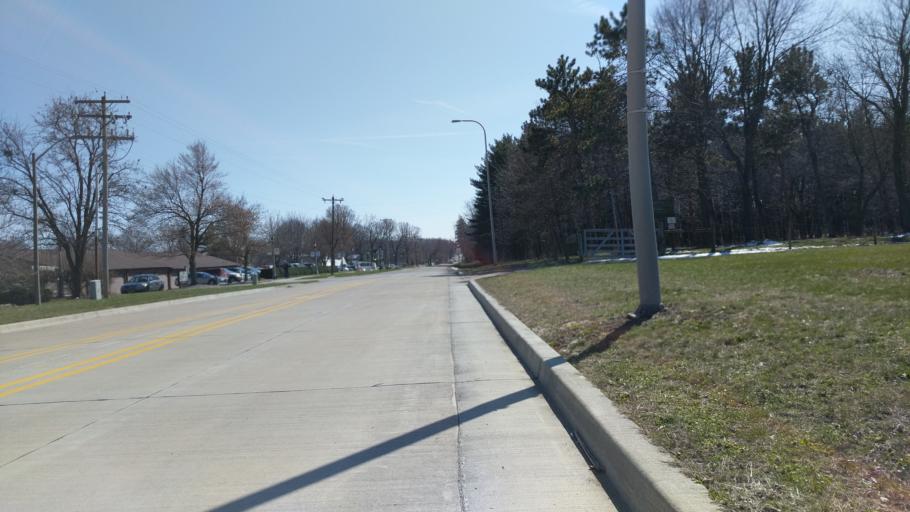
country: US
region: Illinois
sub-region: Champaign County
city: Urbana
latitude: 40.0829
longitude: -88.2095
